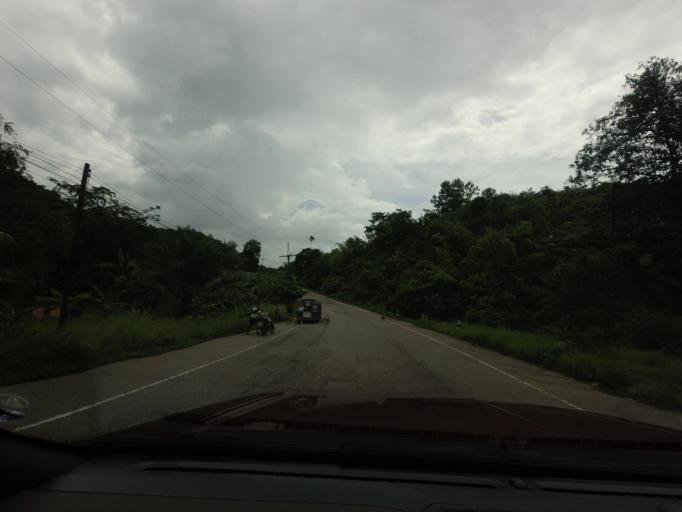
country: TH
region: Narathiwat
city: Sukhirin
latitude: 5.9815
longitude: 101.6927
